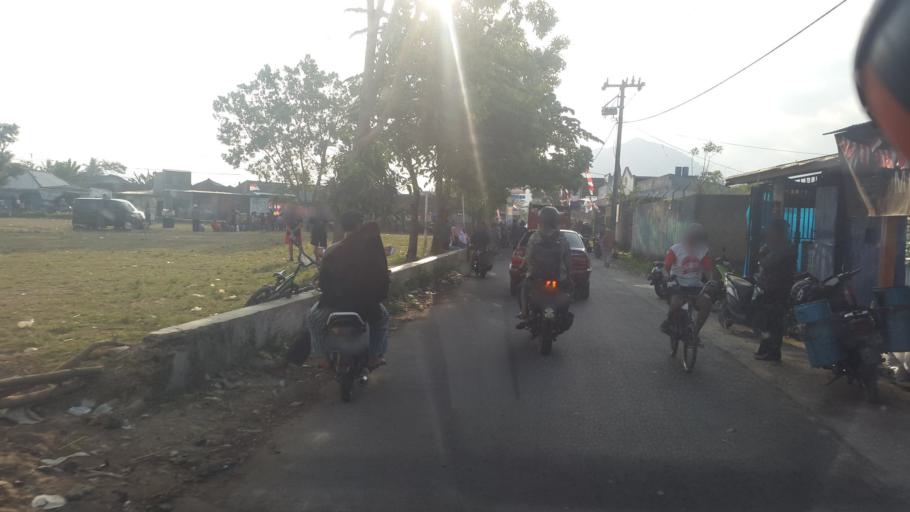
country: ID
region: West Java
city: Cicurug
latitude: -6.8195
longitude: 106.7331
